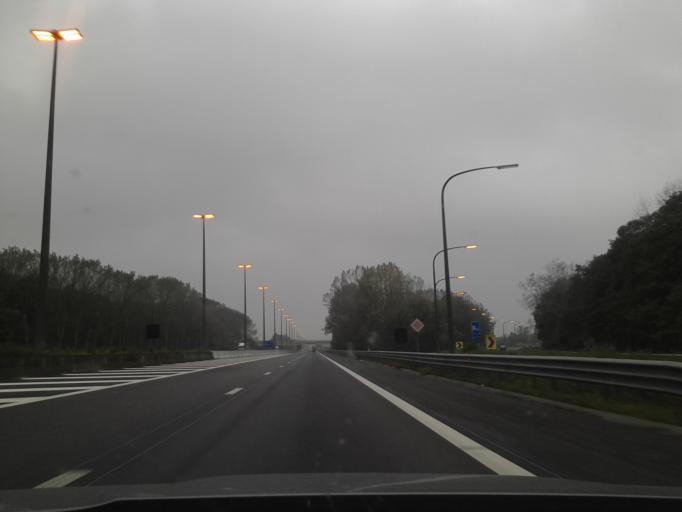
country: BE
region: Wallonia
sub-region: Province du Hainaut
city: Boussu
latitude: 50.4515
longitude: 3.7644
